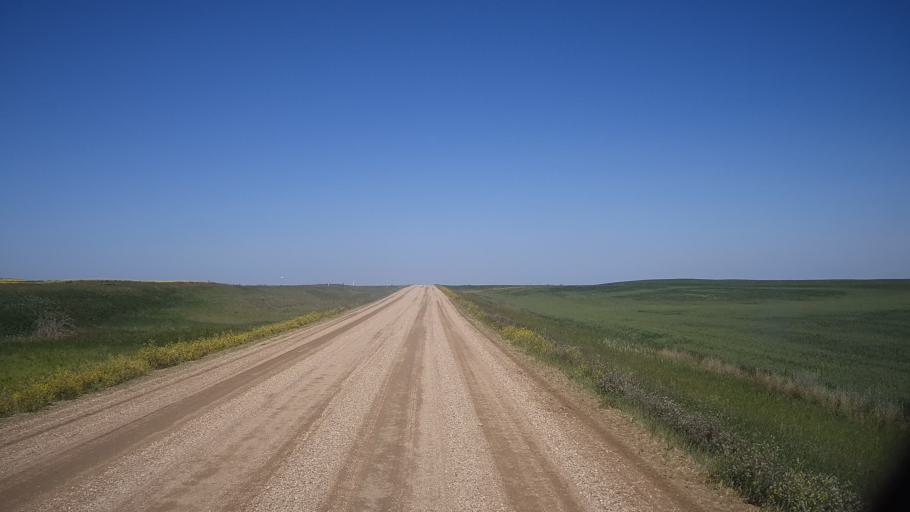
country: CA
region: Saskatchewan
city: Watrous
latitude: 51.8513
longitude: -105.9367
